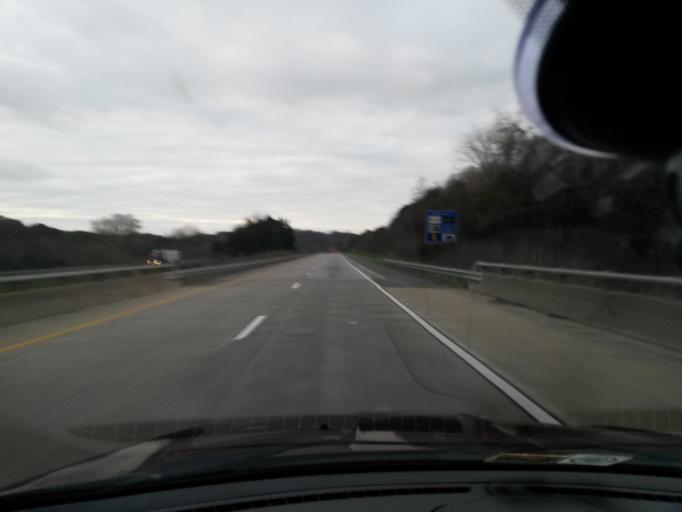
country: US
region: Virginia
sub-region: Rockbridge County
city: East Lexington
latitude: 37.8257
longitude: -79.4434
